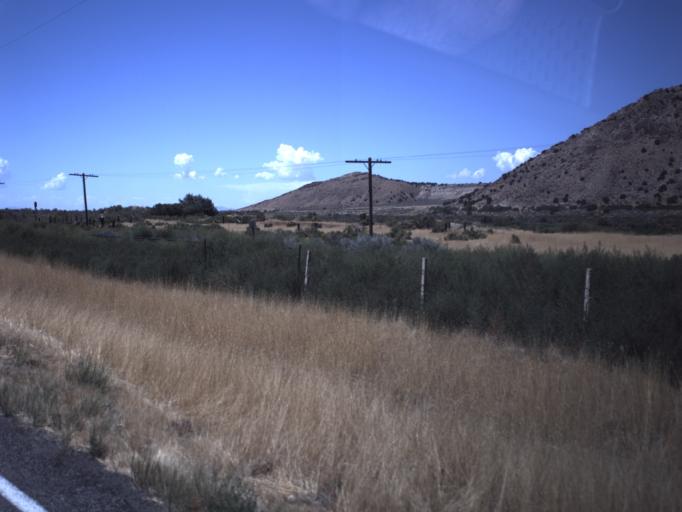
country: US
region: Utah
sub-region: Millard County
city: Delta
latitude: 39.5407
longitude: -112.2443
